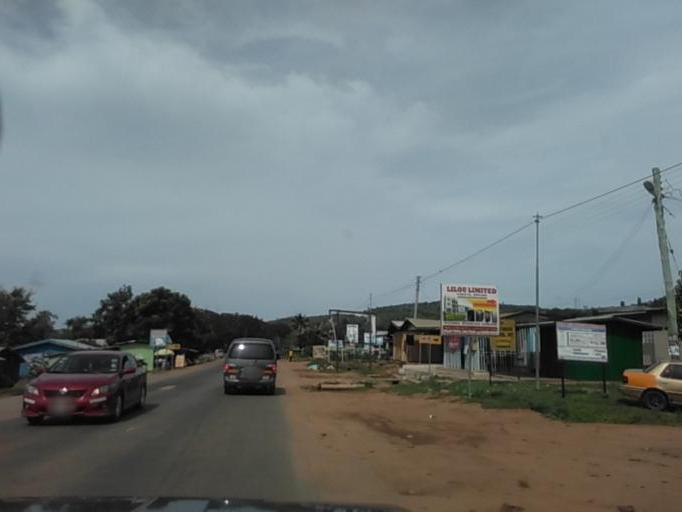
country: GH
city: Akropong
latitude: 6.2289
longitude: 0.0895
